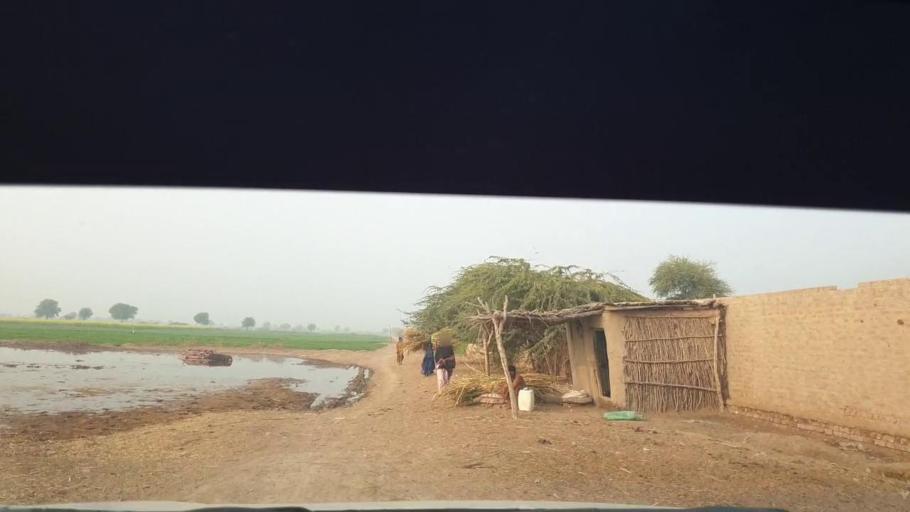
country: PK
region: Sindh
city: Berani
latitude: 25.8441
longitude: 68.8985
